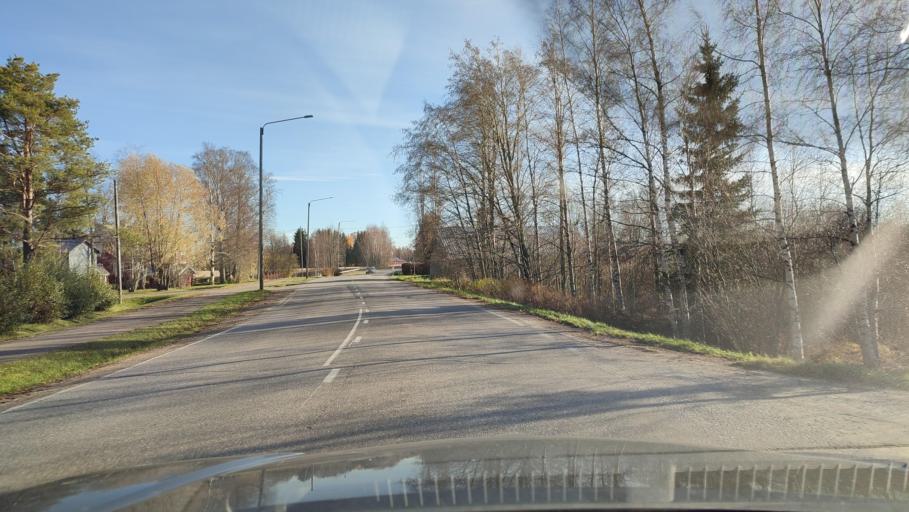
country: FI
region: Southern Ostrobothnia
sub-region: Suupohja
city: Teuva
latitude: 62.4756
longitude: 21.7097
